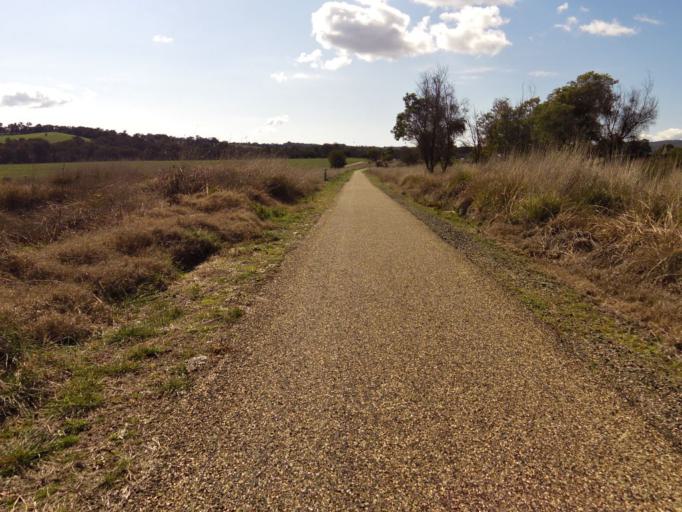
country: AU
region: Victoria
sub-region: Wangaratta
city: Wangaratta
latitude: -36.3970
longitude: 146.6526
